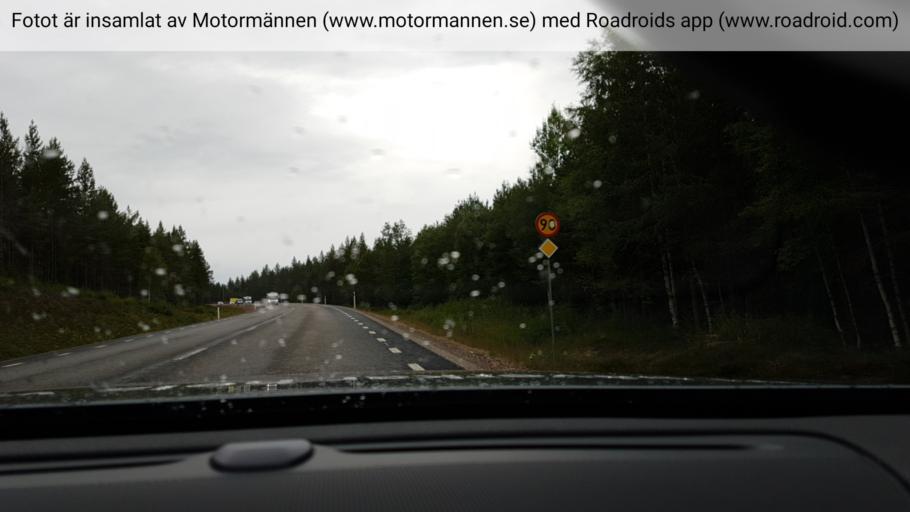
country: SE
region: Dalarna
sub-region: Rattviks Kommun
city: Raettvik
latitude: 60.8173
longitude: 15.2585
